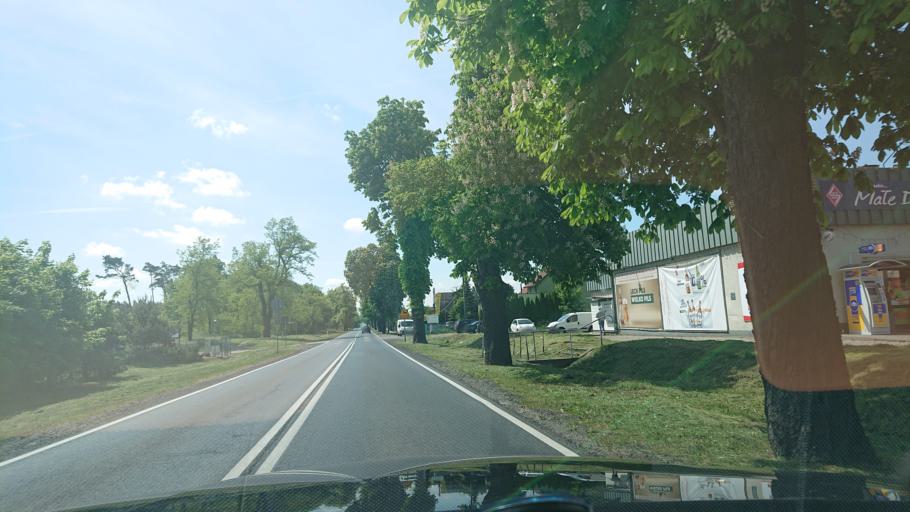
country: PL
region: Greater Poland Voivodeship
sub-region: Powiat gnieznienski
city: Gniezno
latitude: 52.5072
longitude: 17.5948
